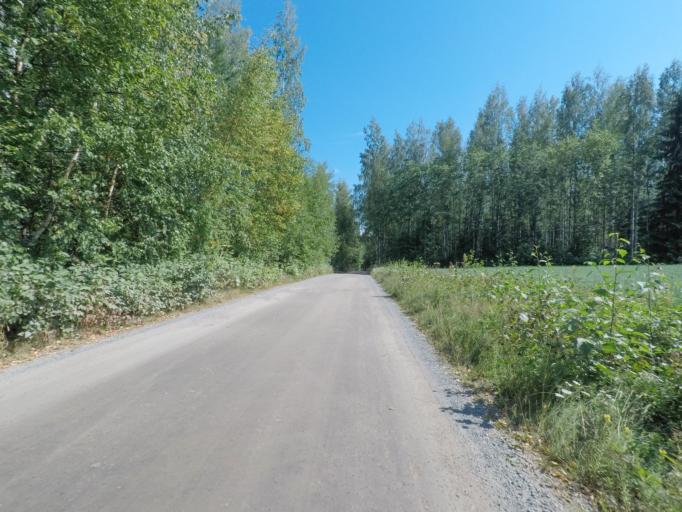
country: FI
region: Southern Savonia
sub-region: Mikkeli
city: Puumala
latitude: 61.4266
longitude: 28.0309
